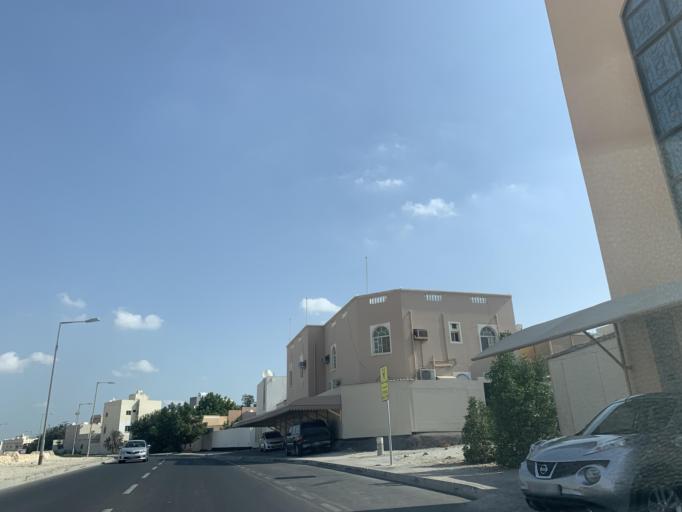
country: BH
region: Central Governorate
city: Madinat Hamad
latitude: 26.1388
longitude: 50.5026
